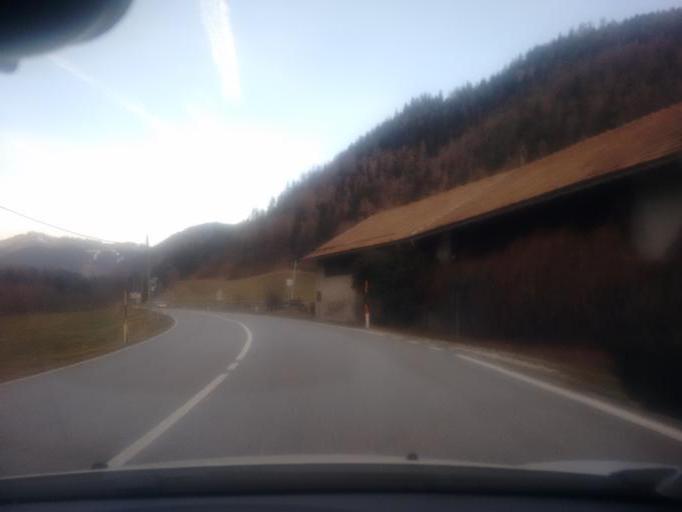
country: IT
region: Trentino-Alto Adige
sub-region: Bolzano
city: Campo di Trens
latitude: 46.8542
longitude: 11.5169
